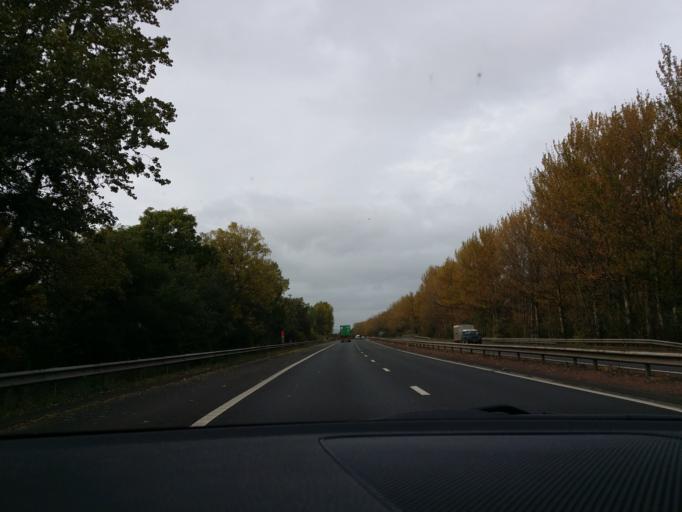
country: GB
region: Scotland
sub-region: Falkirk
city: Grangemouth
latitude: 56.0067
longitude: -3.7394
